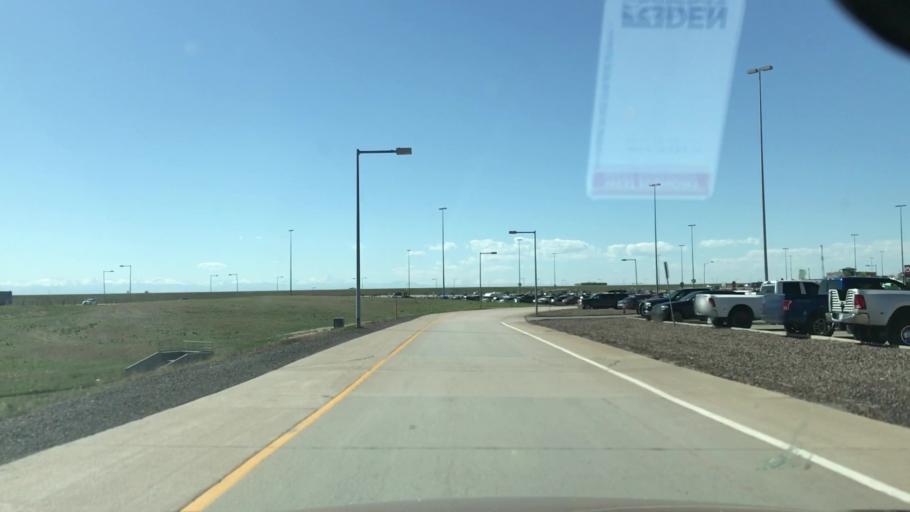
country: US
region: Colorado
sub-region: Weld County
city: Lochbuie
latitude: 39.8447
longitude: -104.6779
